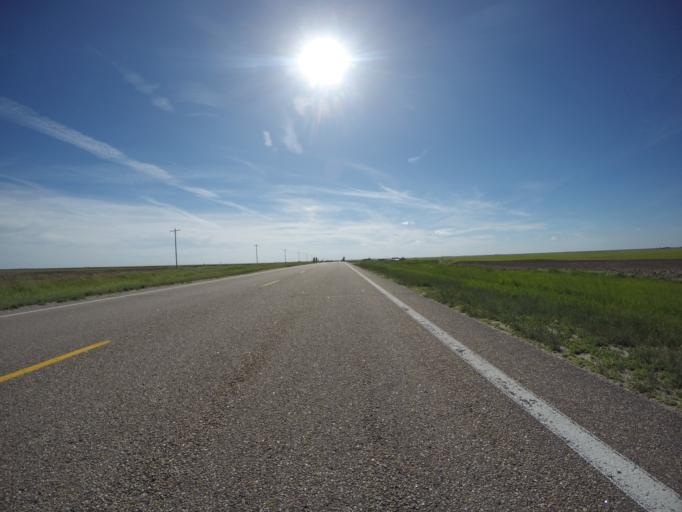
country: US
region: Kansas
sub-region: Cheyenne County
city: Saint Francis
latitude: 39.7566
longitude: -102.0053
